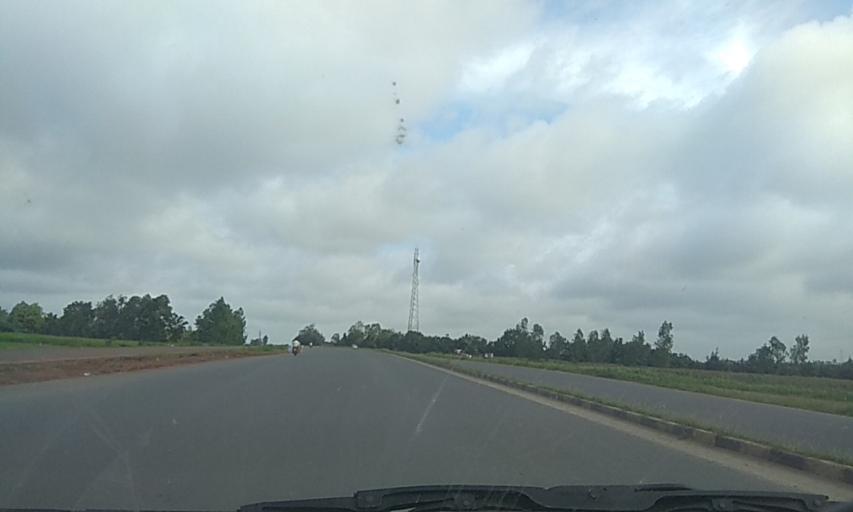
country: IN
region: Karnataka
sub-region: Haveri
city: Shiggaon
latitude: 15.0559
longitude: 75.1667
